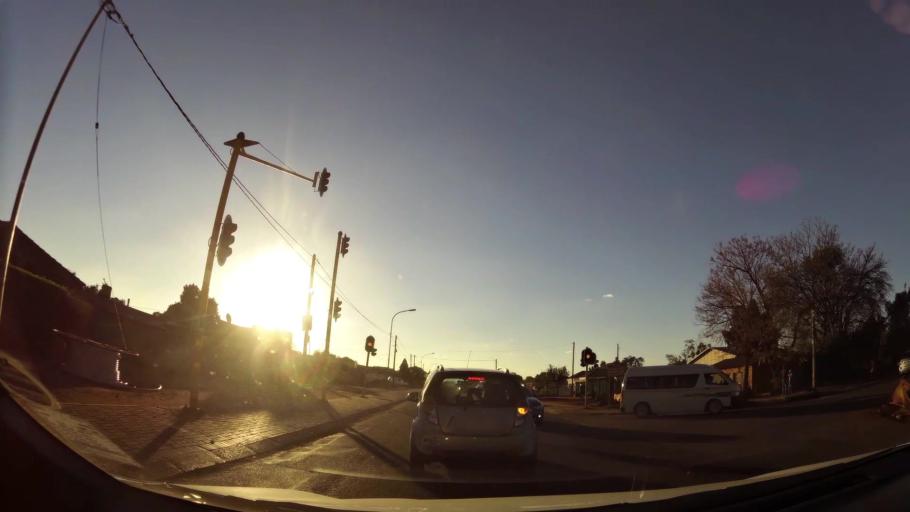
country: ZA
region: Limpopo
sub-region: Waterberg District Municipality
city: Mokopane
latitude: -24.1484
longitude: 28.9787
